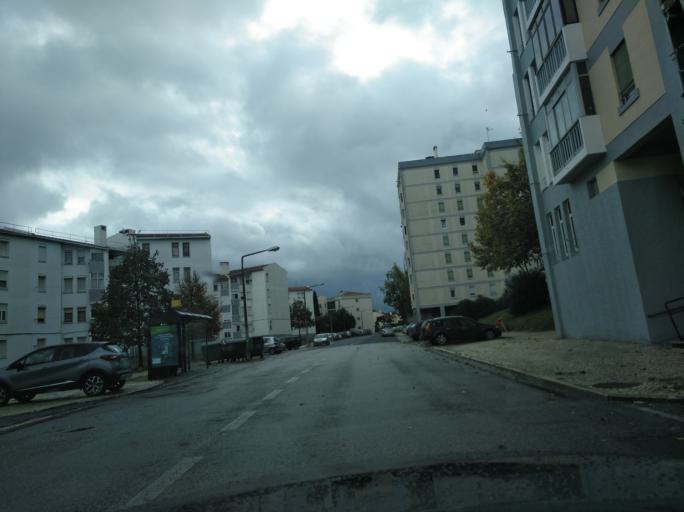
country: PT
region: Lisbon
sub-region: Loures
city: Moscavide
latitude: 38.7608
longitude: -9.1062
